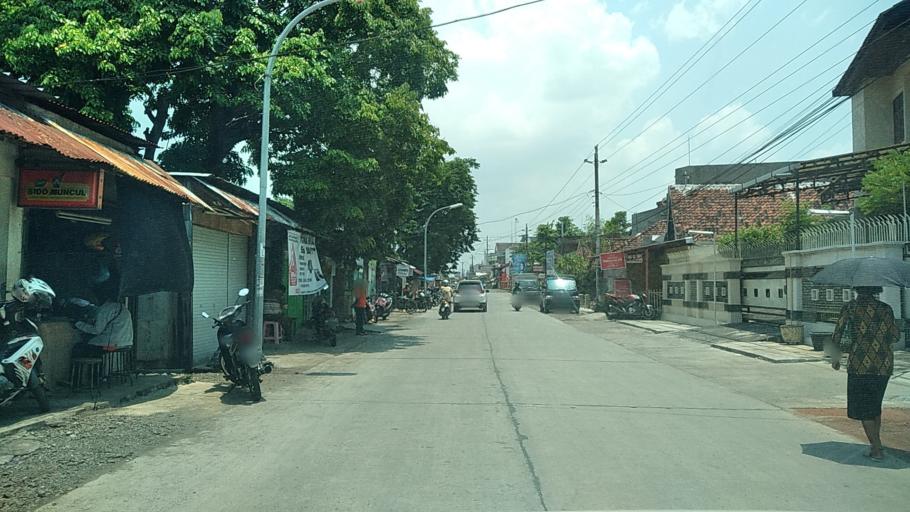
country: ID
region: Central Java
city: Semarang
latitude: -6.9755
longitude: 110.4366
